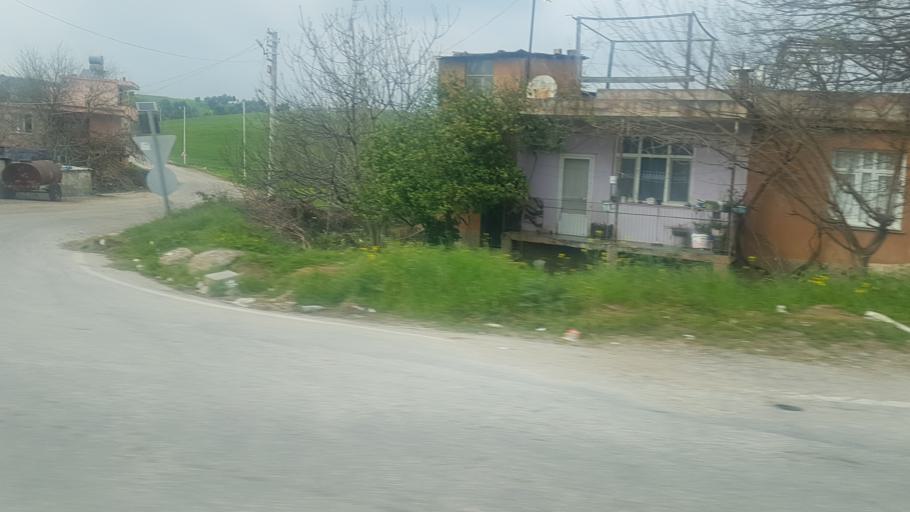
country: TR
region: Adana
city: Seyhan
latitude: 37.0576
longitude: 35.2263
